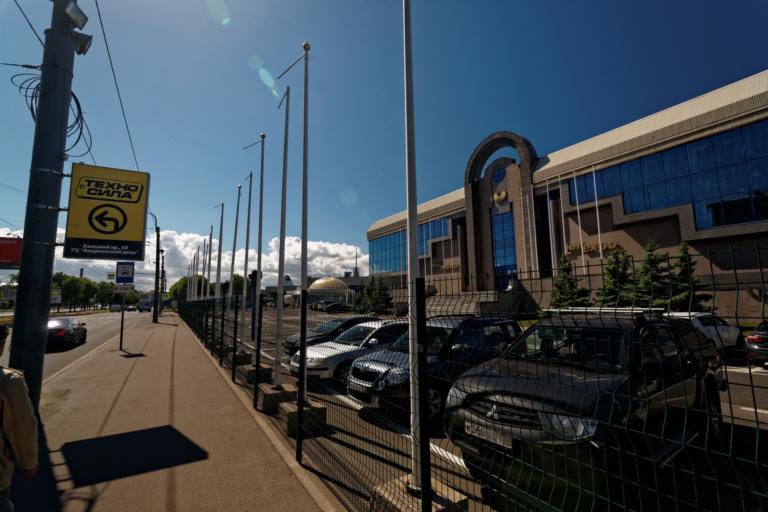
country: RU
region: St.-Petersburg
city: Vasyl'evsky Ostrov
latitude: 59.9303
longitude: 30.2368
